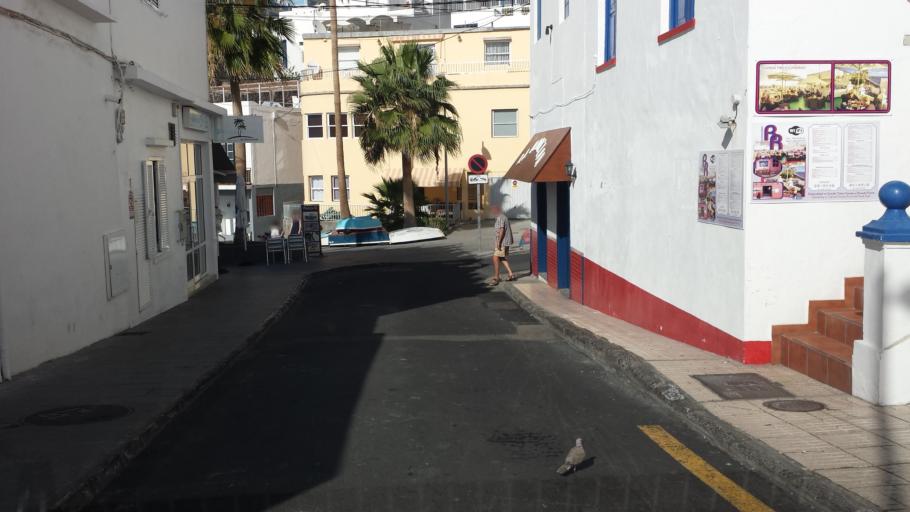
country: ES
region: Canary Islands
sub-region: Provincia de Santa Cruz de Tenerife
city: Tazacorte
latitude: 28.5866
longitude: -17.9105
